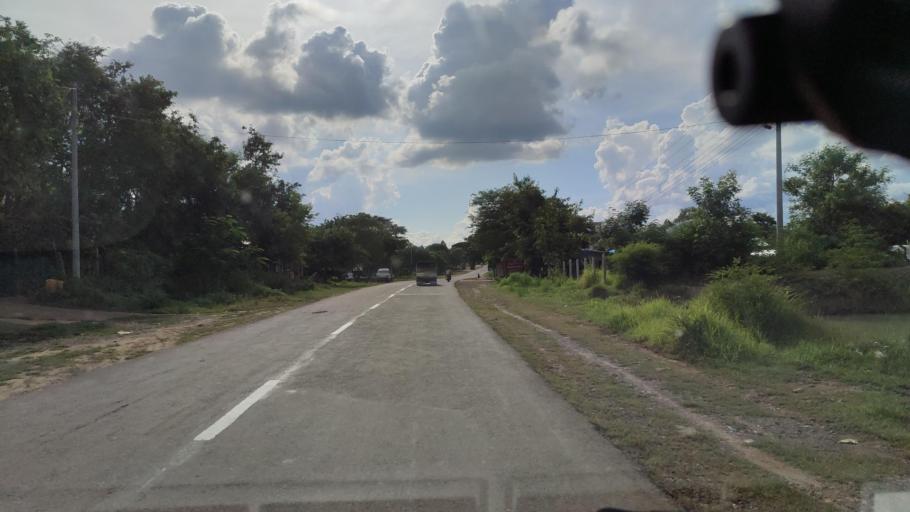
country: MM
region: Mandalay
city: Meiktila
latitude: 20.8140
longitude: 95.4328
